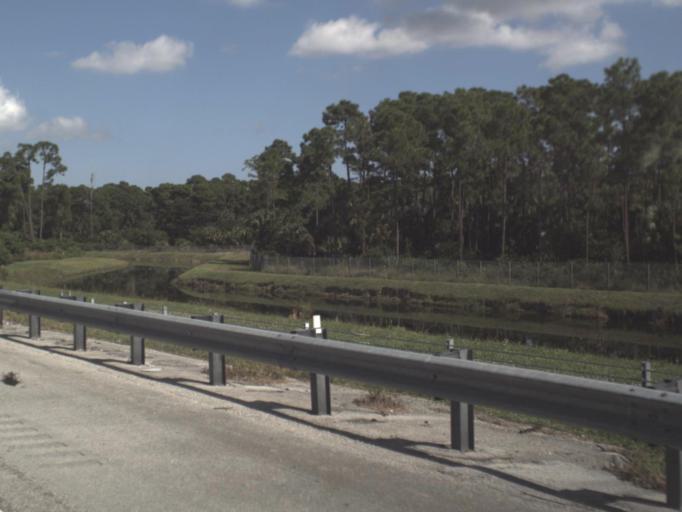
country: US
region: Florida
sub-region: Palm Beach County
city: Palm Beach Gardens
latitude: 26.7721
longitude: -80.1330
